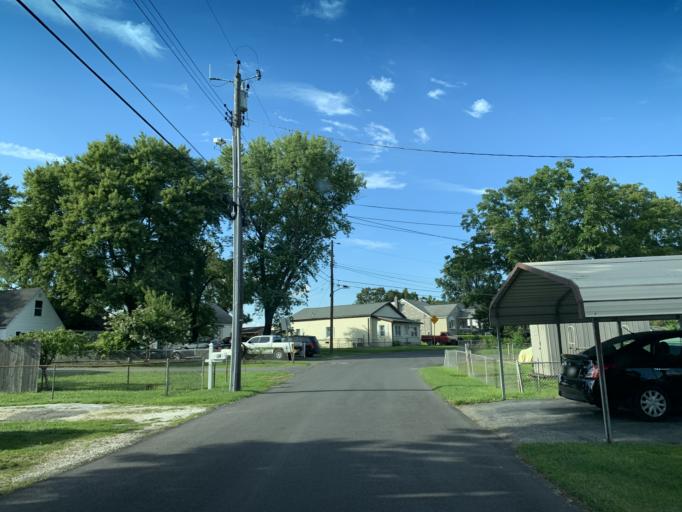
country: US
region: Maryland
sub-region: Baltimore County
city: Essex
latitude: 39.3051
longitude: -76.4893
